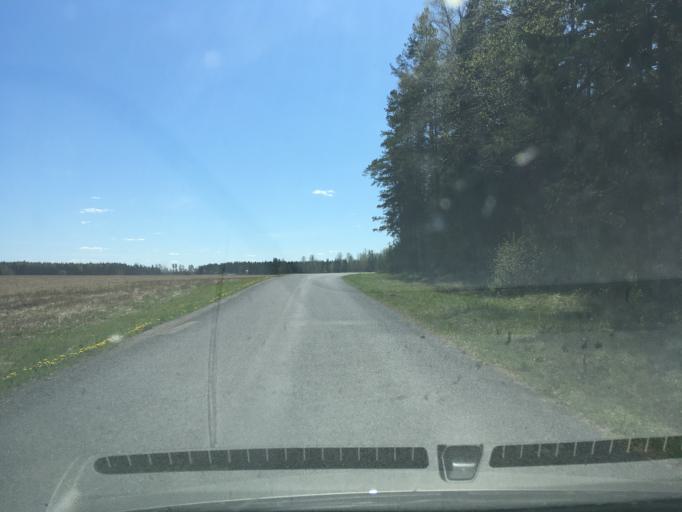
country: EE
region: Harju
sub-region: Raasiku vald
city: Raasiku
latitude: 59.2200
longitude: 25.1816
